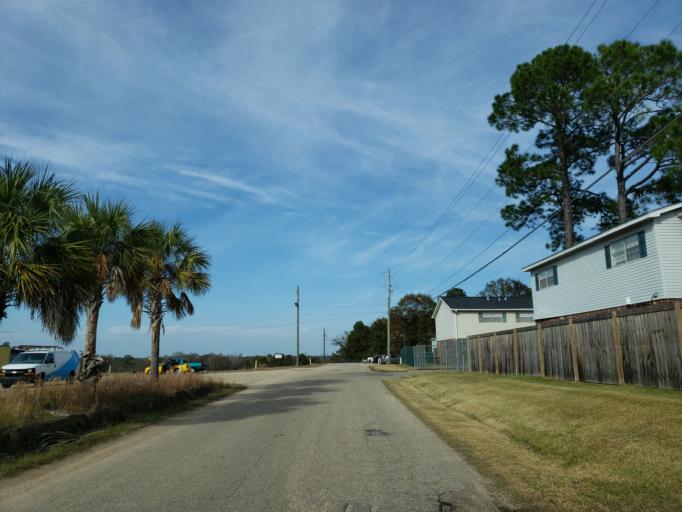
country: US
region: Mississippi
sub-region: Forrest County
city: Glendale
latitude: 31.3507
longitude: -89.3353
